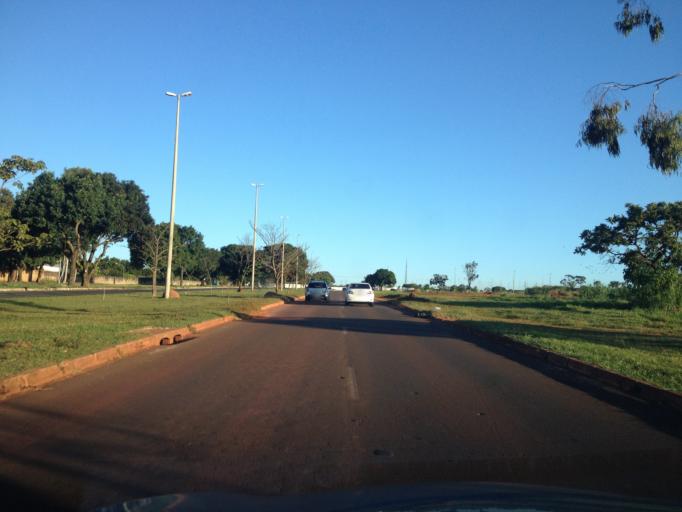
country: BR
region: Federal District
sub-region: Brasilia
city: Brasilia
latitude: -15.7620
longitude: -47.8989
